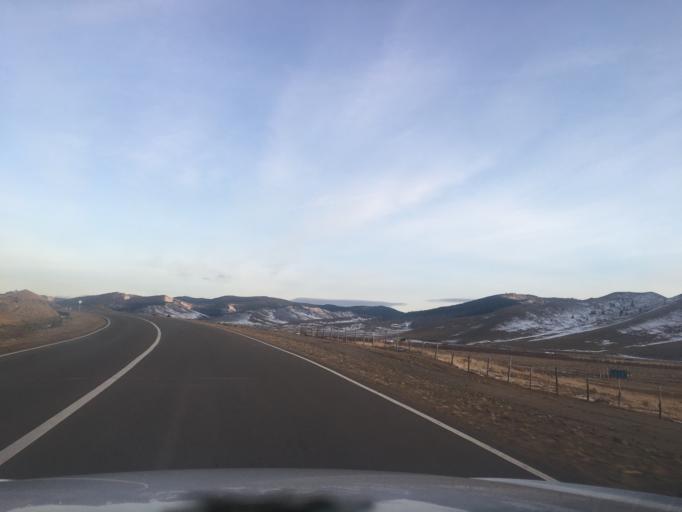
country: MN
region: Central Aimak
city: Mandal
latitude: 48.1092
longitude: 106.7134
